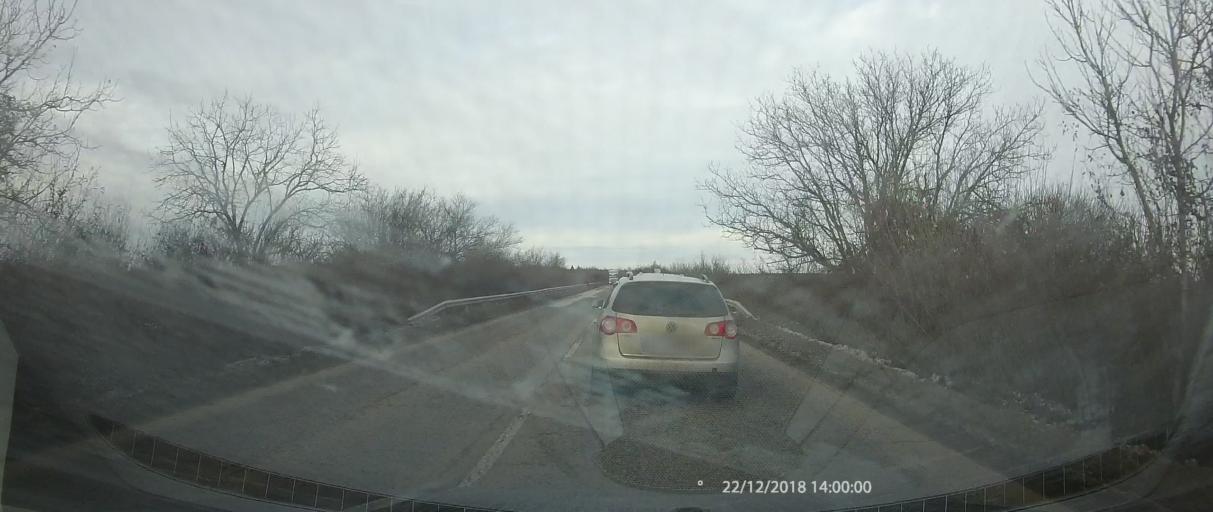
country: BG
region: Pleven
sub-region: Obshtina Dolni Dubnik
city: Dolni Dubnik
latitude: 43.3556
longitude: 24.3435
